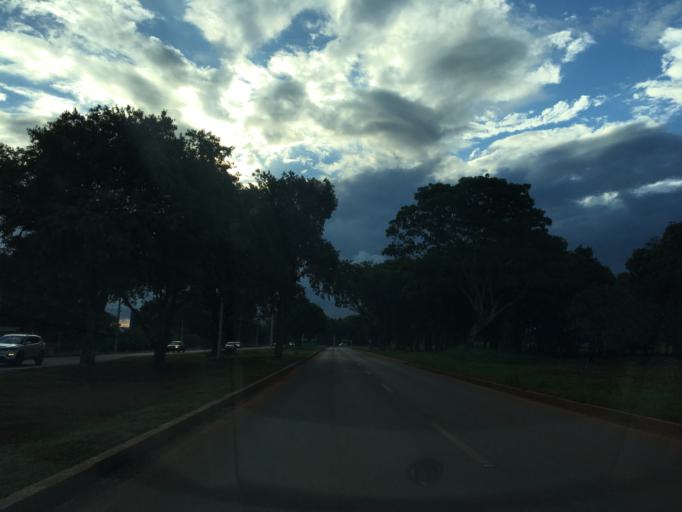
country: BR
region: Federal District
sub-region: Brasilia
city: Brasilia
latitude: -15.8165
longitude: -47.8645
